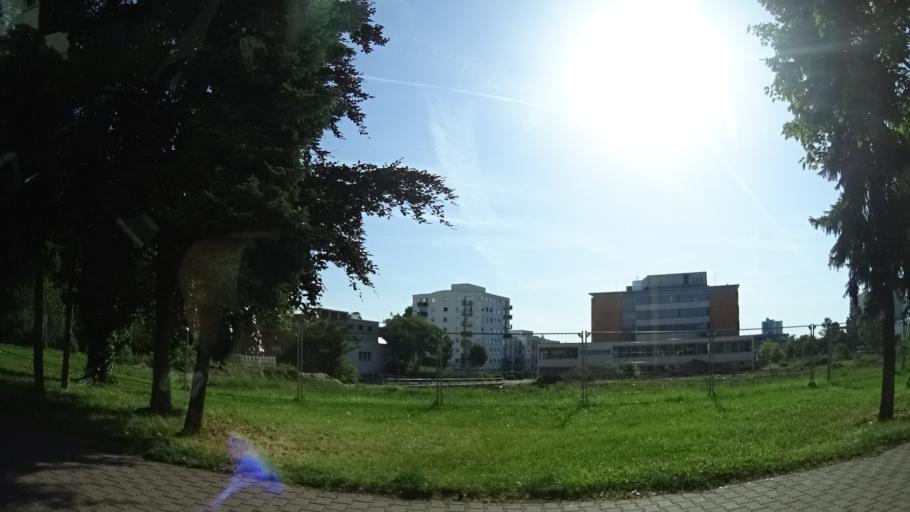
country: DE
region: Hesse
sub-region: Regierungsbezirk Darmstadt
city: Bad Homburg vor der Hoehe
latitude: 50.2223
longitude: 8.6073
